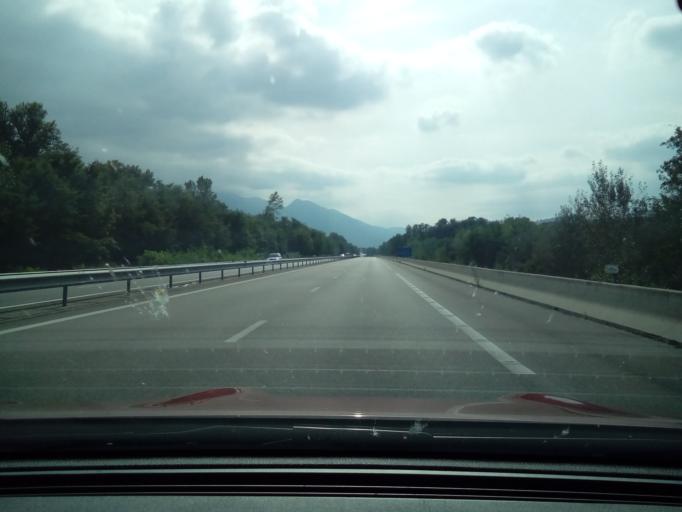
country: FR
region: Rhone-Alpes
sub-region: Departement de l'Isere
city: Saint-Quentin-sur-Isere
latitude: 45.2623
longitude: 5.5157
